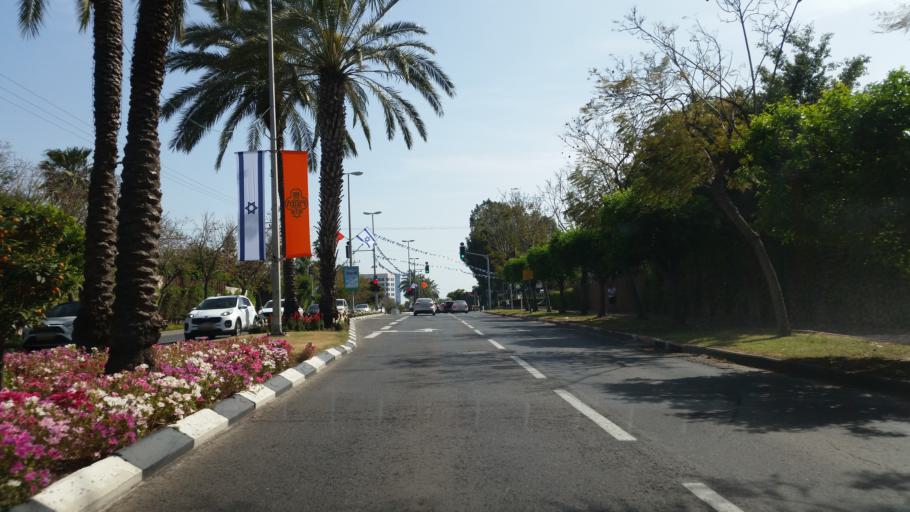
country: IL
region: Central District
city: Ra'anana
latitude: 32.1906
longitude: 34.8552
